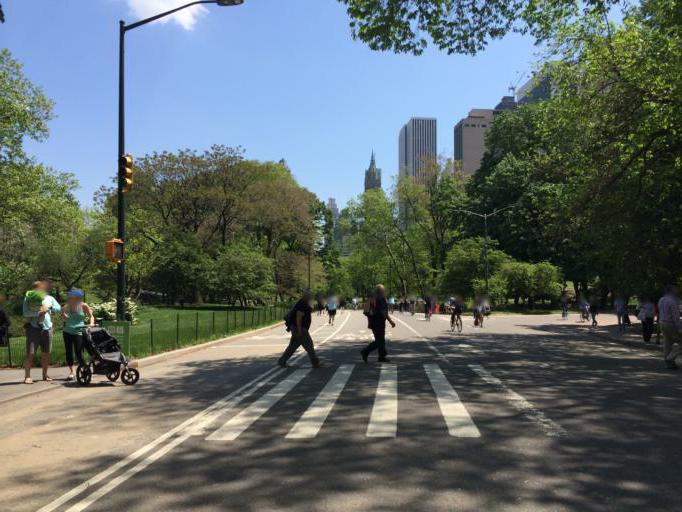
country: US
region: New York
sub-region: New York County
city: Manhattan
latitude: 40.7680
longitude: -73.9790
